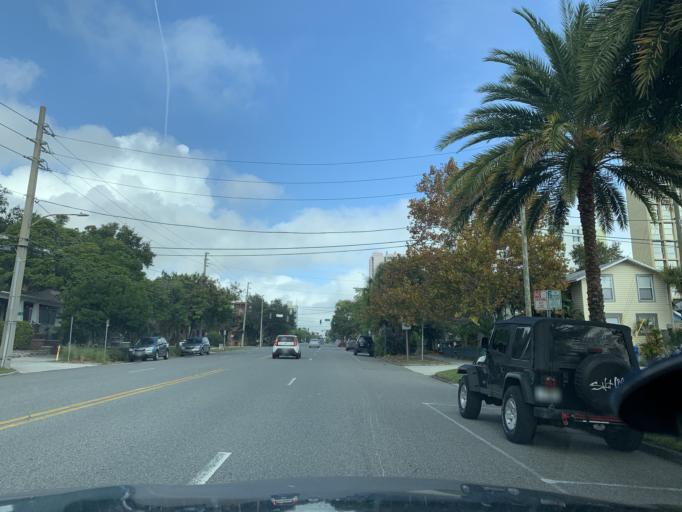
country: US
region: Florida
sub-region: Pinellas County
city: Saint Petersburg
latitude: 27.7675
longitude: -82.6416
